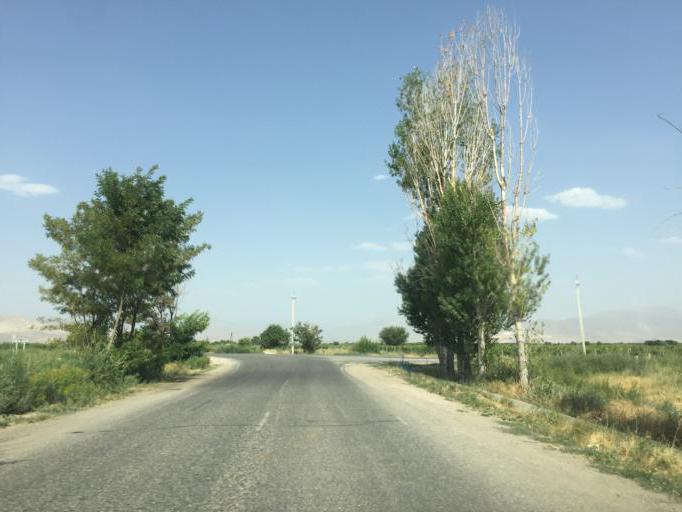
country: AM
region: Ararat
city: Yeghegnavan
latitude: 39.8839
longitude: 44.5903
